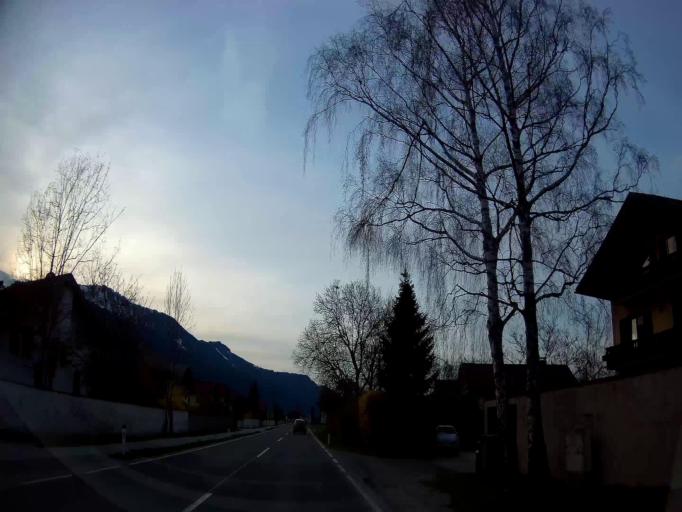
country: AT
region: Salzburg
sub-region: Politischer Bezirk Hallein
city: Kuchl
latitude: 47.6174
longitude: 13.1606
